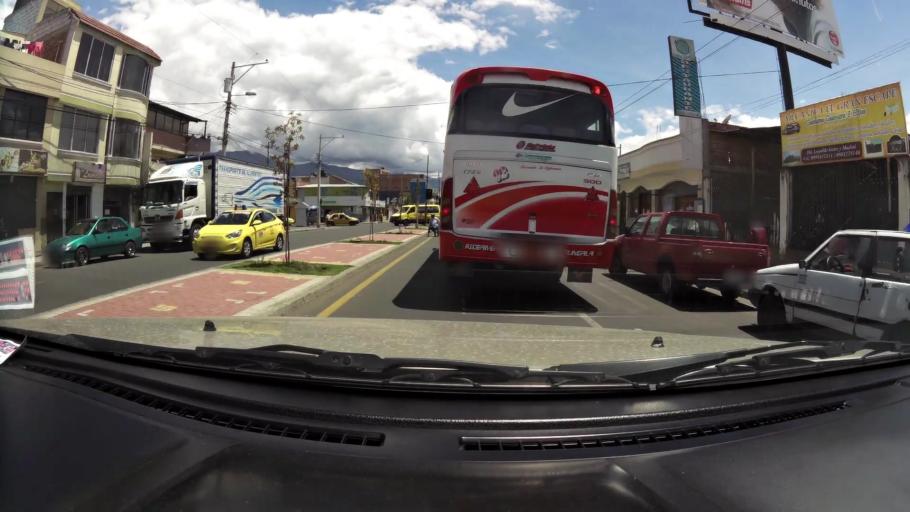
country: EC
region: Chimborazo
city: Riobamba
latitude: -1.6842
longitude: -78.6359
